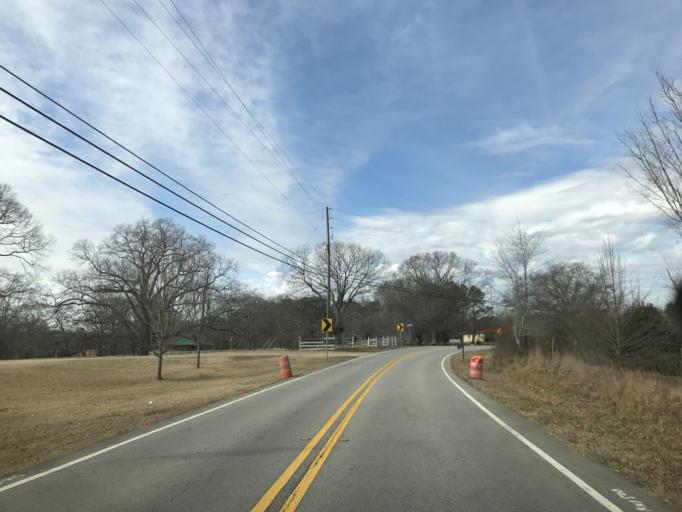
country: US
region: Georgia
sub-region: Douglas County
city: Douglasville
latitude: 33.8019
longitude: -84.8399
